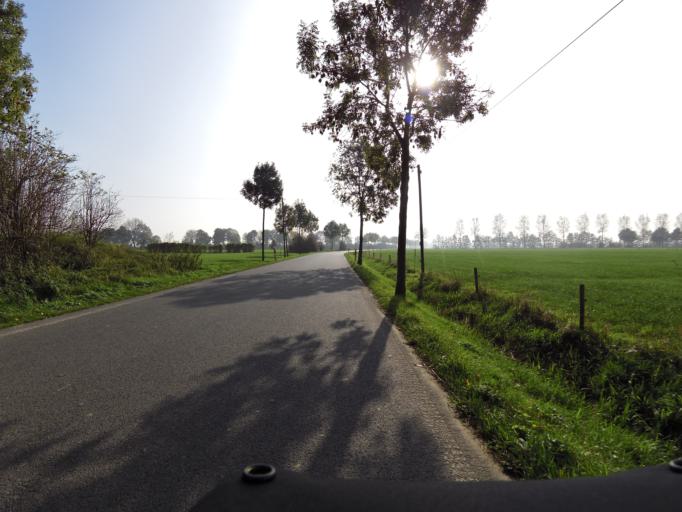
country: DE
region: North Rhine-Westphalia
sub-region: Regierungsbezirk Dusseldorf
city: Kranenburg
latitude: 51.8374
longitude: 6.0347
